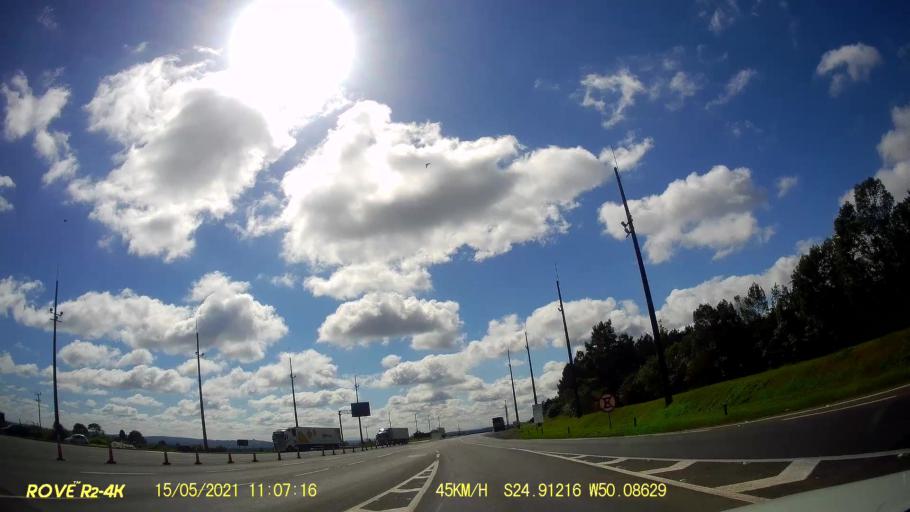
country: BR
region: Parana
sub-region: Carambei
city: Carambei
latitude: -24.9121
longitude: -50.0861
